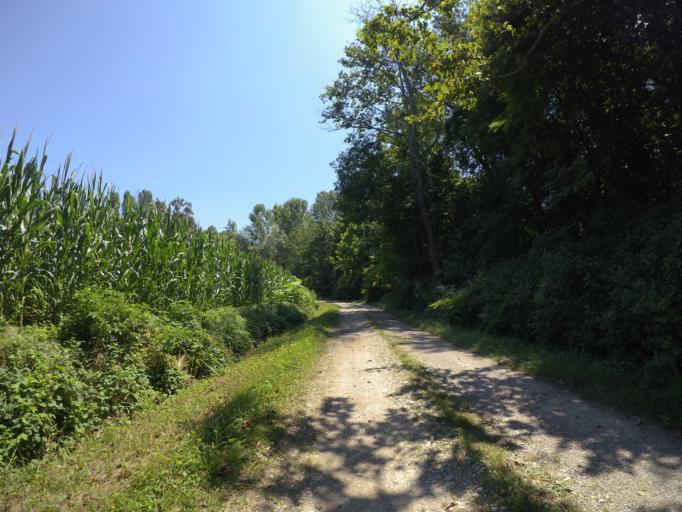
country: IT
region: Friuli Venezia Giulia
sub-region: Provincia di Udine
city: Bertiolo
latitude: 45.9272
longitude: 13.0804
